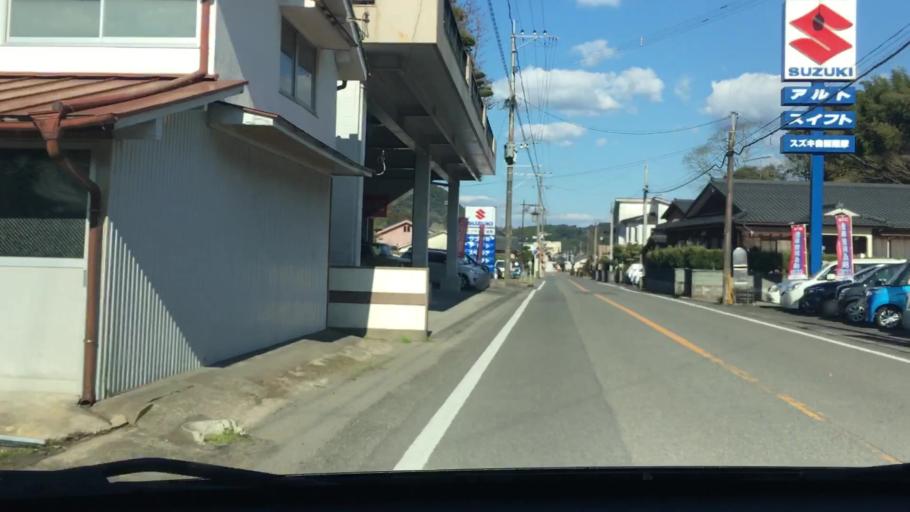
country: JP
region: Kagoshima
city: Satsumasendai
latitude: 31.7855
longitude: 130.4025
